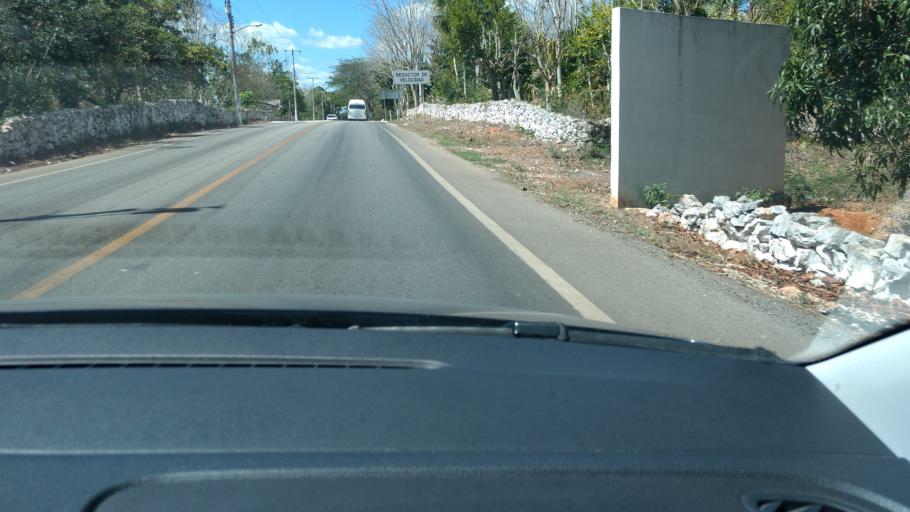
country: MX
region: Yucatan
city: Tzucacab
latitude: 20.0773
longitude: -89.0604
